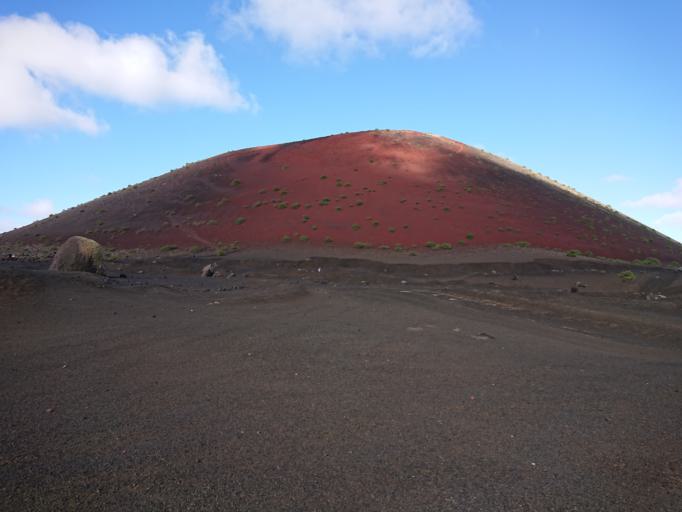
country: ES
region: Canary Islands
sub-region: Provincia de Las Palmas
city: Tias
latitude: 29.0036
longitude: -13.6759
